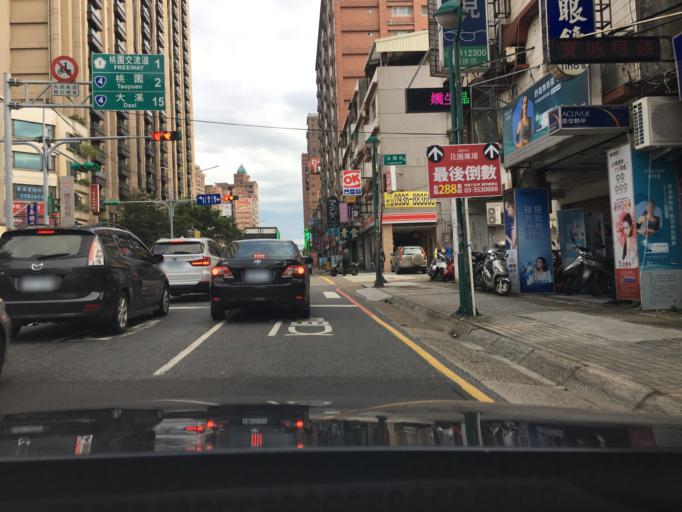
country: TW
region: Taiwan
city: Taoyuan City
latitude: 25.0462
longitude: 121.2927
